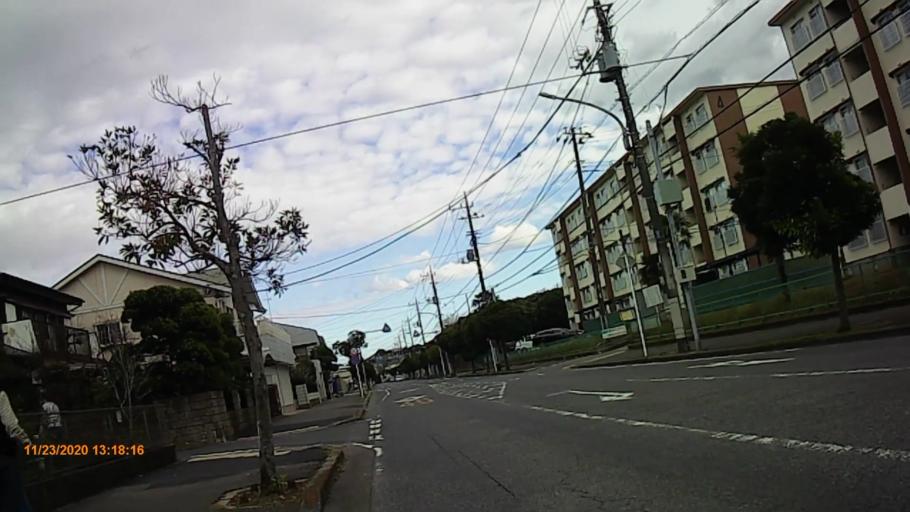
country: JP
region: Chiba
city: Yotsukaido
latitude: 35.6160
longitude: 140.1928
